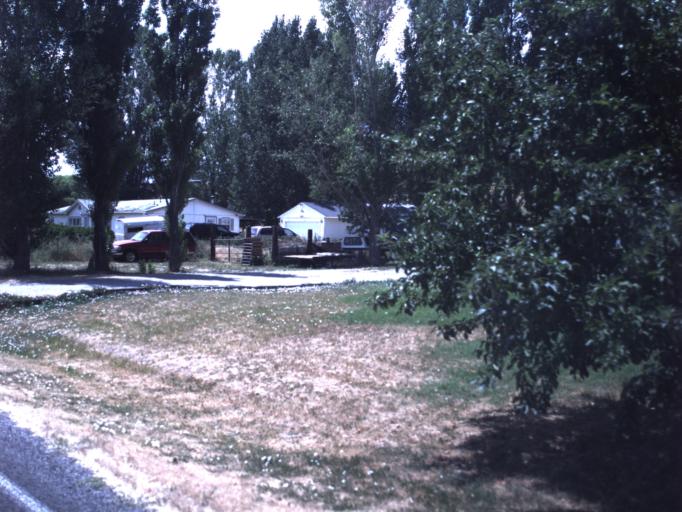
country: US
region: Utah
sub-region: Box Elder County
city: Tremonton
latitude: 41.6774
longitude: -112.2968
